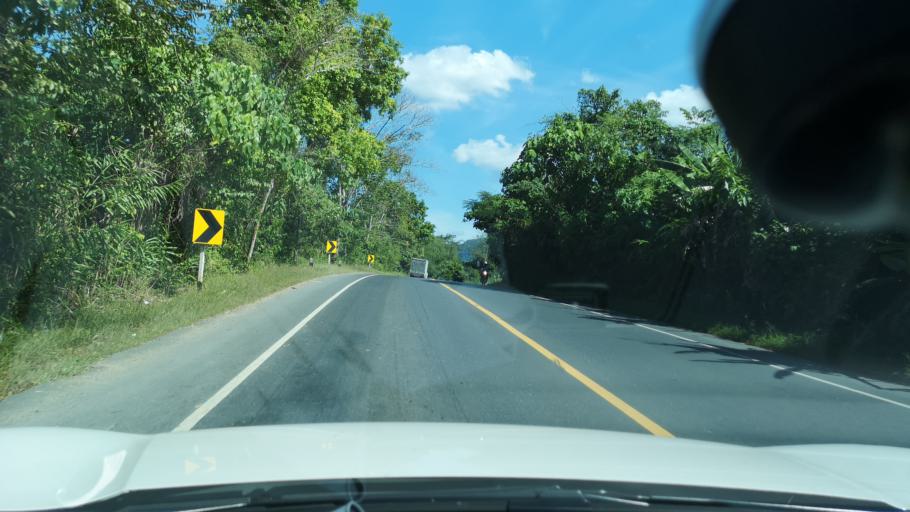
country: TH
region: Phangnga
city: Phang Nga
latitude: 8.5332
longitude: 98.5127
